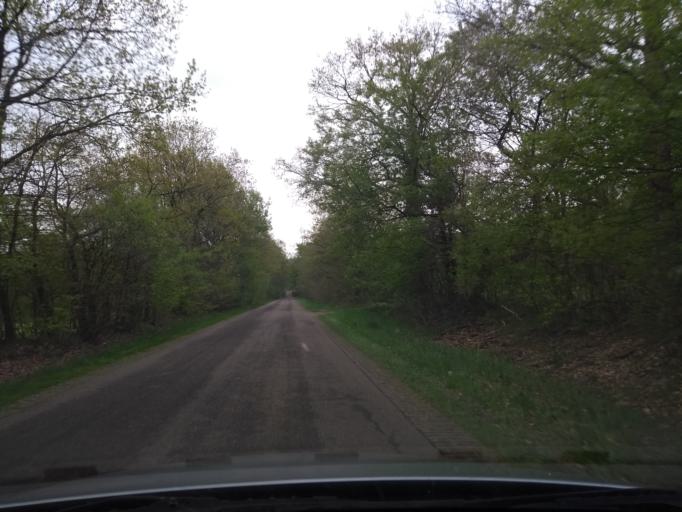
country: DE
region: Lower Saxony
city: Lage
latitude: 52.4241
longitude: 6.9085
